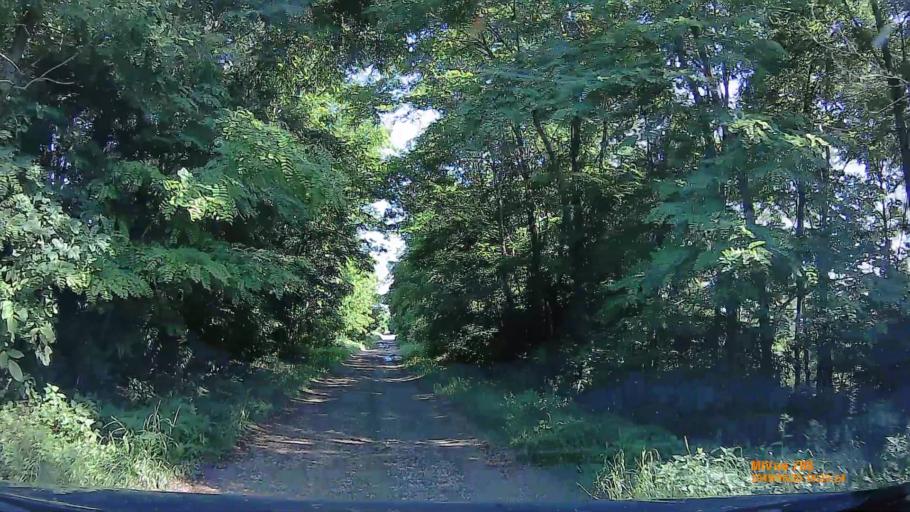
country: HU
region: Baranya
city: Buekkoesd
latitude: 46.1702
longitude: 18.0328
